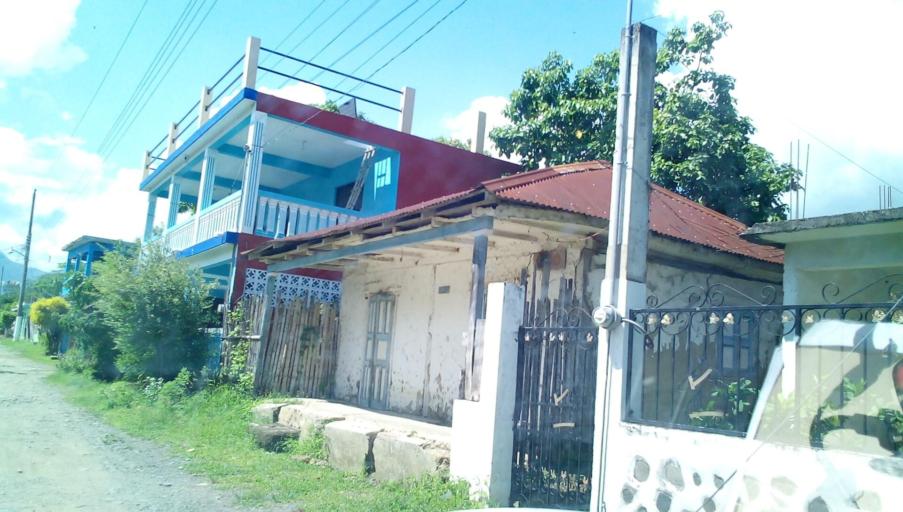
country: MX
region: Veracruz
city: Tamalin
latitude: 21.3667
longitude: -97.8007
